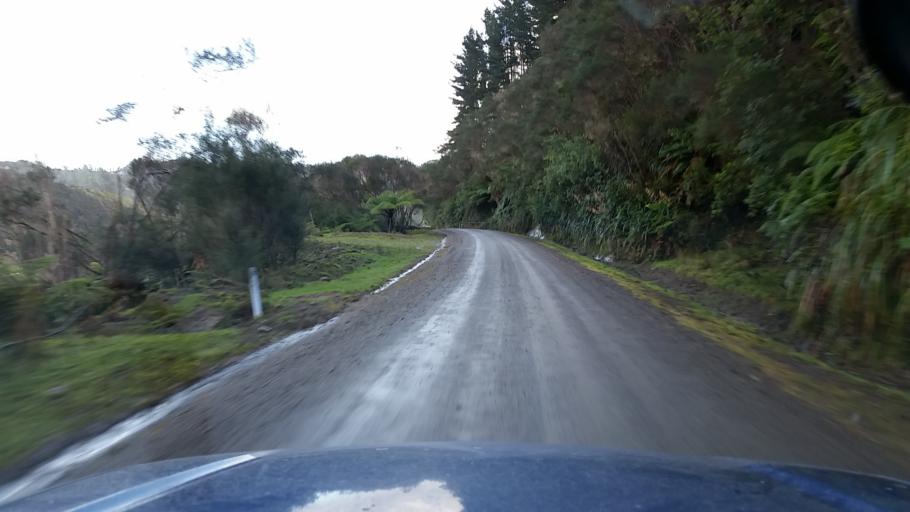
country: NZ
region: Taranaki
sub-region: South Taranaki District
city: Patea
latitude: -39.5567
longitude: 174.5726
